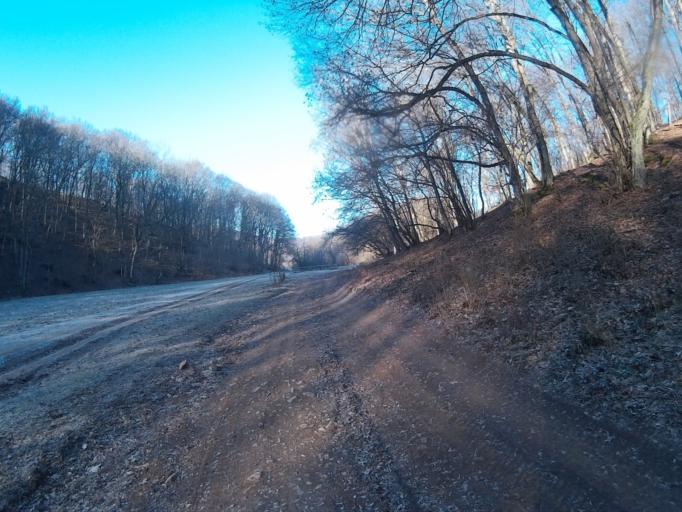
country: HU
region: Borsod-Abauj-Zemplen
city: Rudabanya
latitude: 48.4919
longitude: 20.5457
